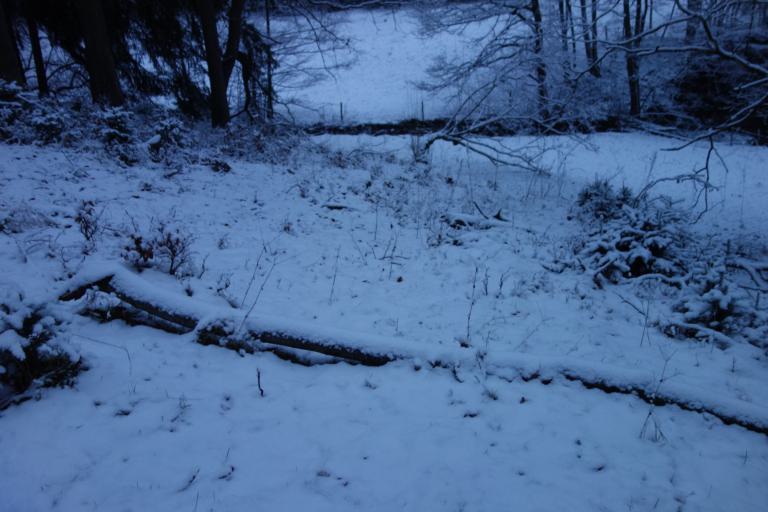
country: DE
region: Saxony
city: Grunhainichen
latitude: 50.7563
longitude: 13.1618
